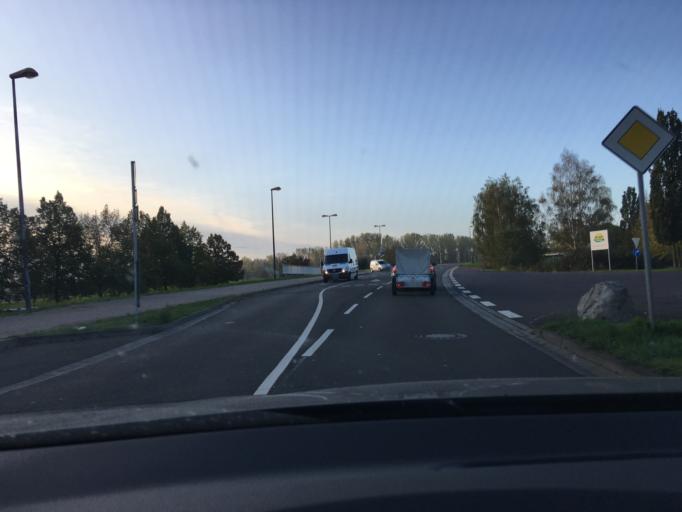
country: DE
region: Saxony
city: Borna
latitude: 51.1124
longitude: 12.4925
